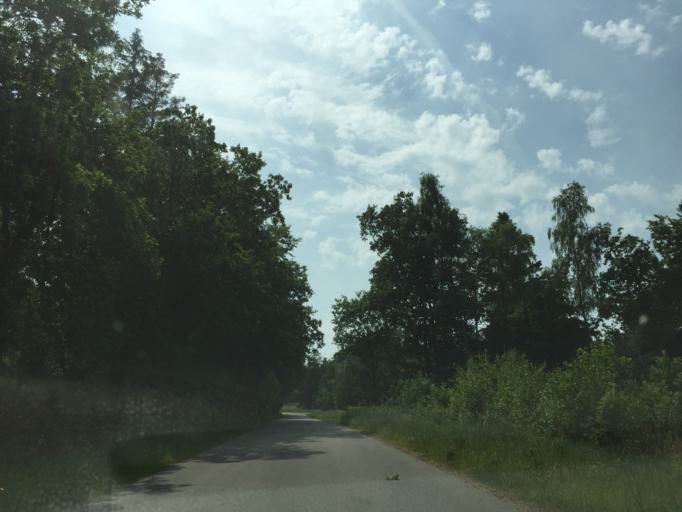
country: DK
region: Central Jutland
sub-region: Silkeborg Kommune
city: Virklund
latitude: 56.0497
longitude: 9.4548
